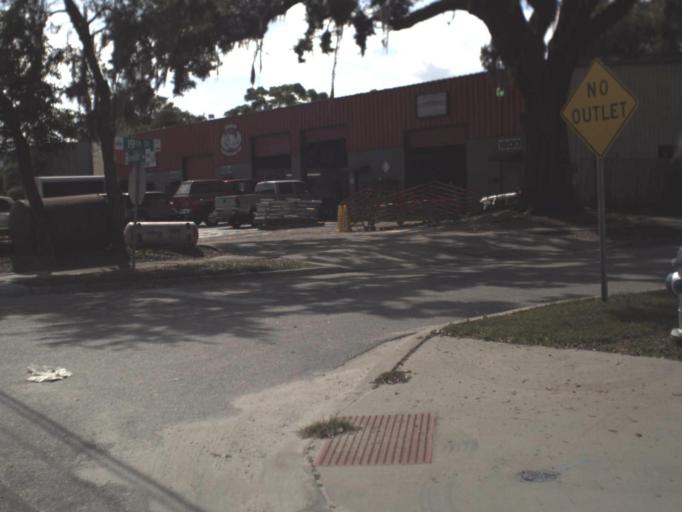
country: US
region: Florida
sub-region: Orange County
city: Orlando
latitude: 28.5221
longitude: -81.3847
